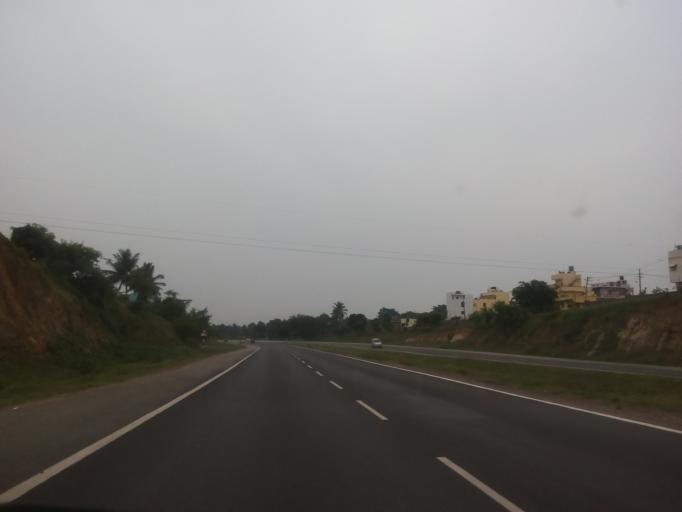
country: IN
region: Karnataka
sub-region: Bangalore Urban
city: Bangalore
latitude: 12.9863
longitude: 77.4716
